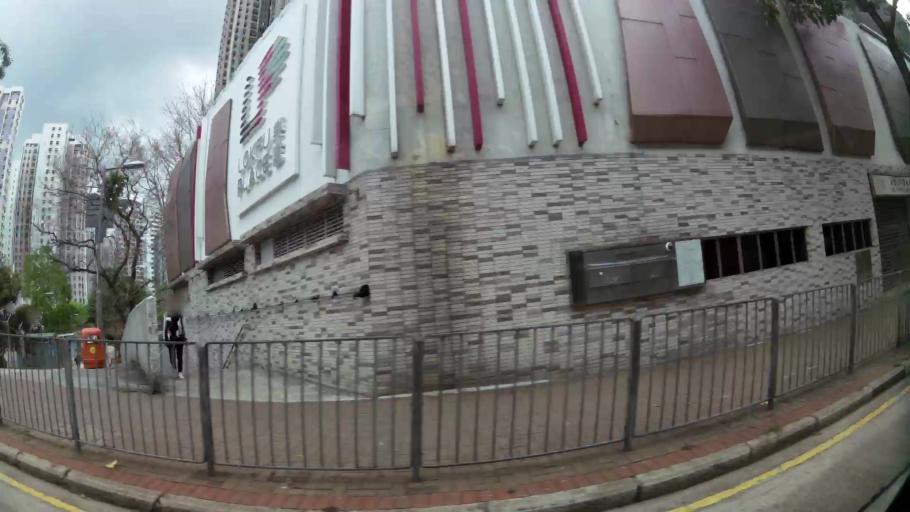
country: HK
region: Wong Tai Sin
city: Wong Tai Sin
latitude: 22.3384
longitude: 114.1855
